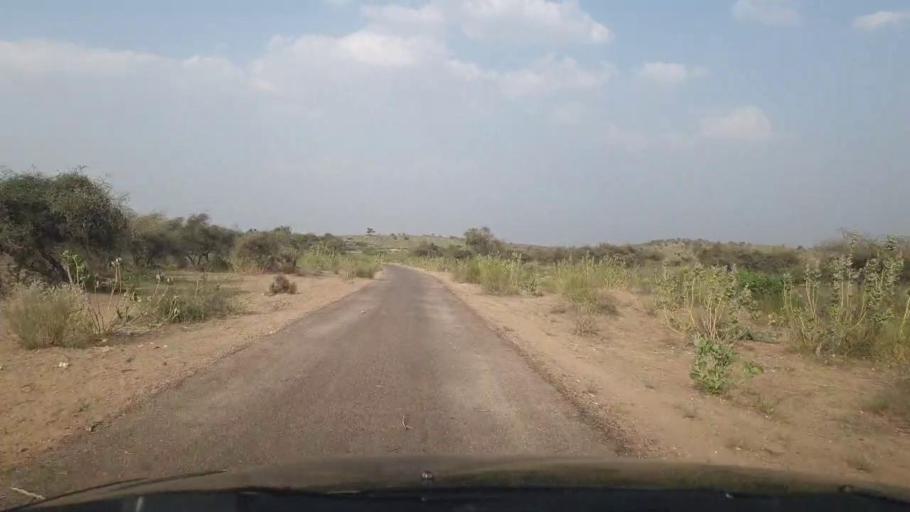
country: PK
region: Sindh
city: Islamkot
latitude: 25.0650
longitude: 70.5646
